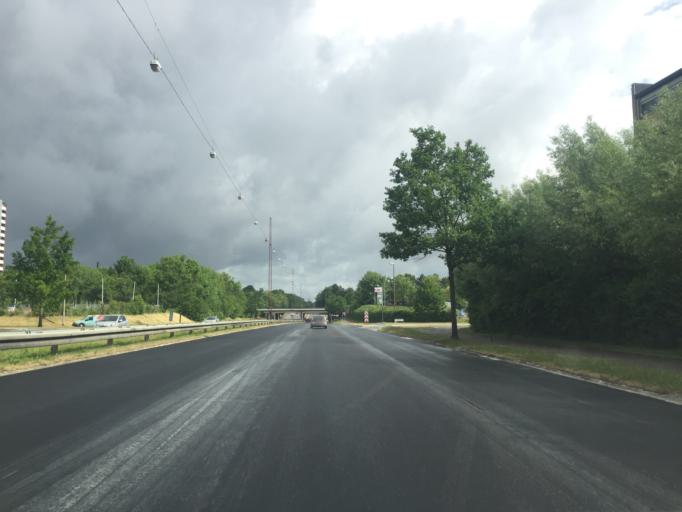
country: DK
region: Capital Region
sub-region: Rodovre Kommune
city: Rodovre
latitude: 55.6618
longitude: 12.4549
